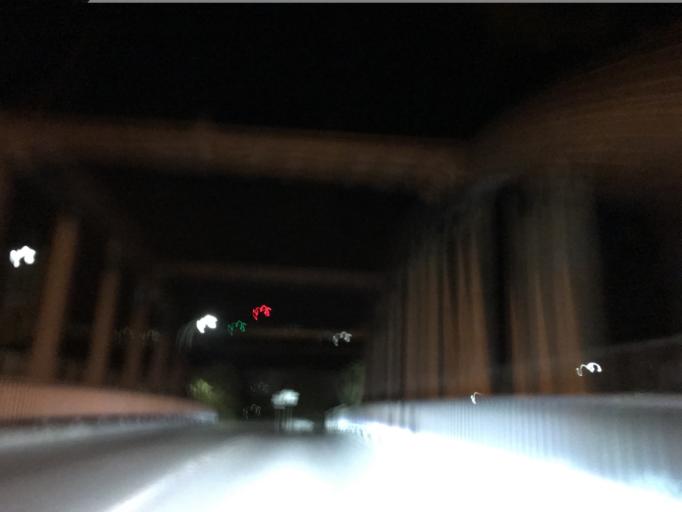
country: FR
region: Auvergne
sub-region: Departement de l'Allier
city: Vichy
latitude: 46.1223
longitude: 3.4321
